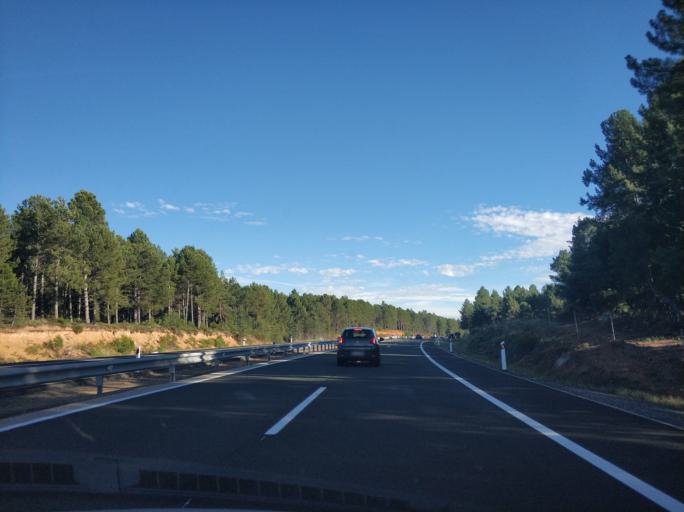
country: ES
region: Castille and Leon
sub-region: Provincia de Leon
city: Cimanes del Tejar
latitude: 42.6764
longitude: -5.7498
